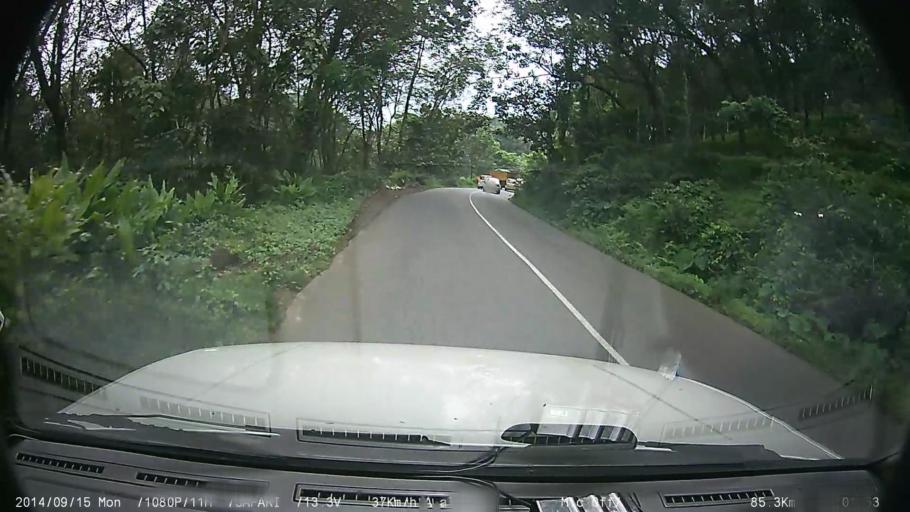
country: IN
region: Kerala
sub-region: Ernakulam
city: Muvattupuzha
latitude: 9.9313
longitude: 76.5762
